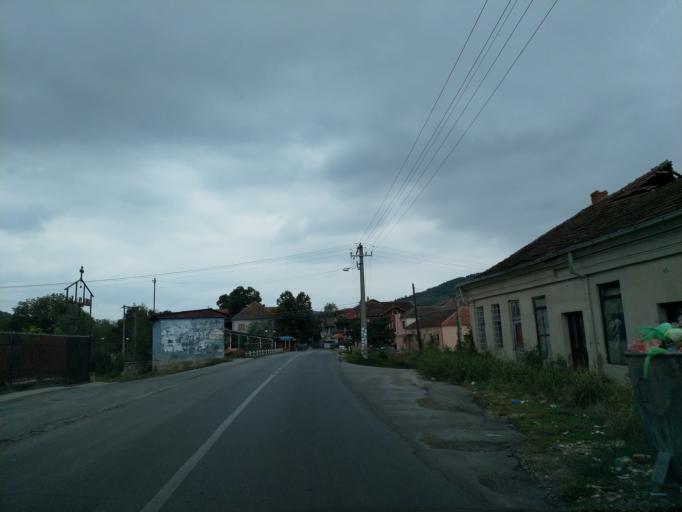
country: RS
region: Central Serbia
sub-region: Pomoravski Okrug
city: Jagodina
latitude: 44.0672
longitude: 21.1788
